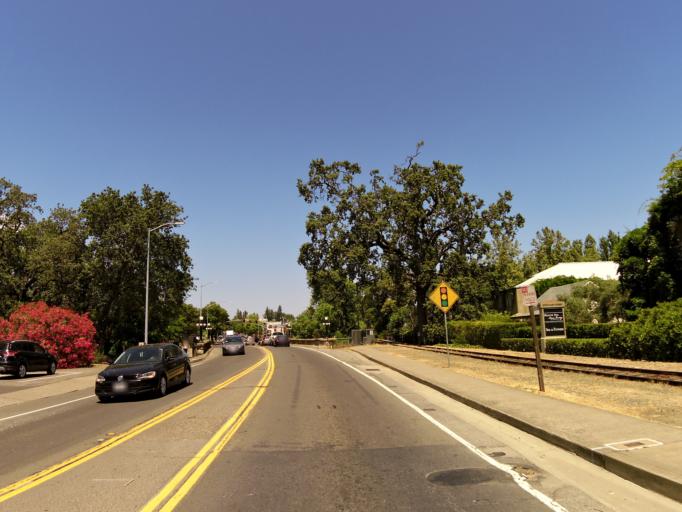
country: US
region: California
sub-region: Napa County
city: Saint Helena
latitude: 38.5023
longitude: -122.4654
